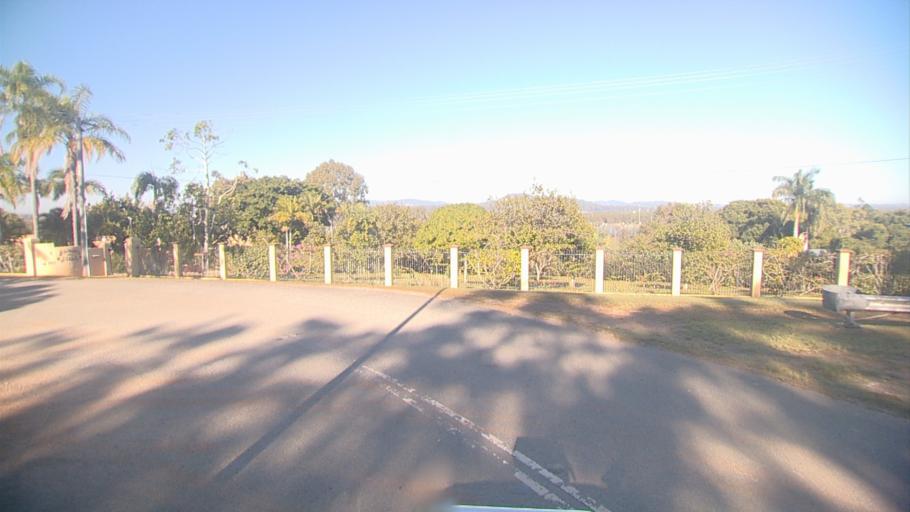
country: AU
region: Queensland
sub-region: Gold Coast
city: Yatala
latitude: -27.6876
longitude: 153.2667
